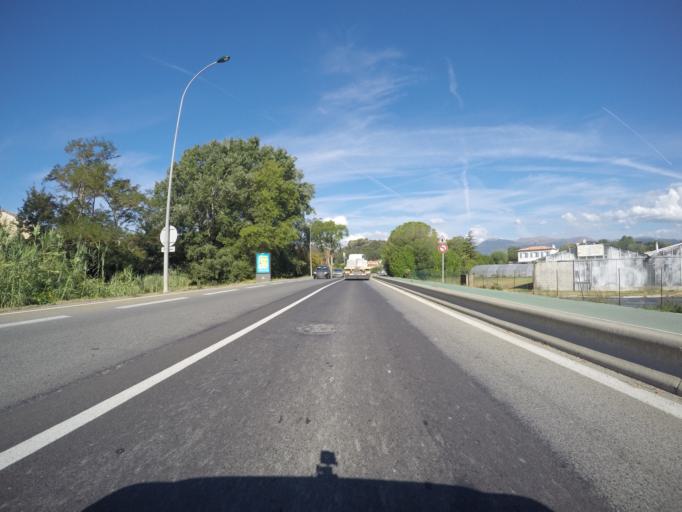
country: FR
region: Provence-Alpes-Cote d'Azur
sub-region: Departement des Alpes-Maritimes
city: Villeneuve-Loubet
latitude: 43.6494
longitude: 7.1324
